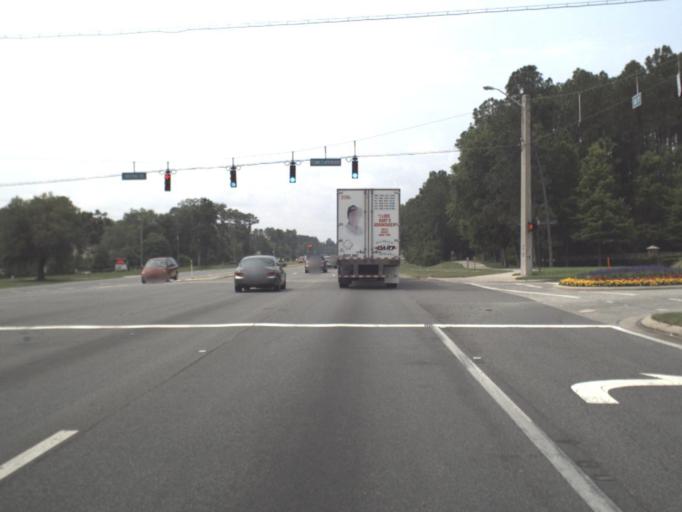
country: US
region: Florida
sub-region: Saint Johns County
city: Fruit Cove
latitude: 30.0695
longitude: -81.7074
